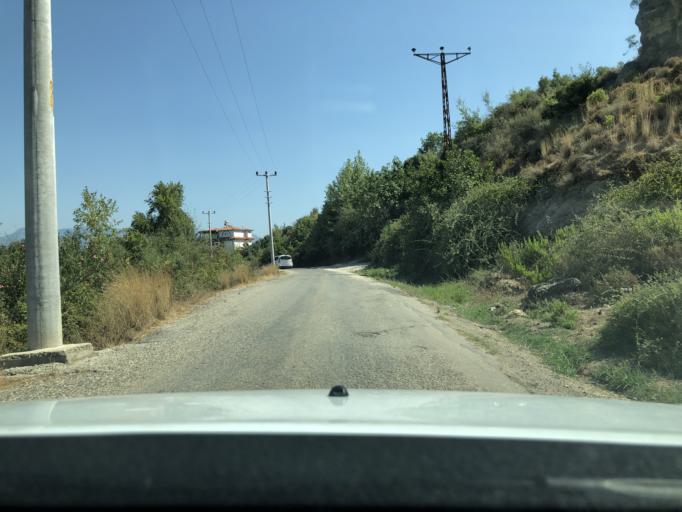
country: TR
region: Antalya
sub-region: Manavgat
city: Manavgat
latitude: 36.8007
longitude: 31.4687
